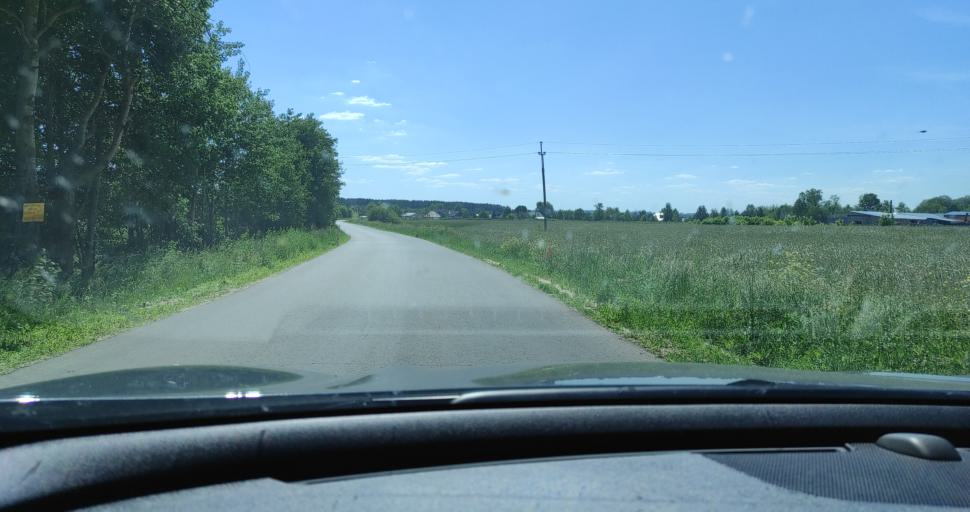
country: RU
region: Rjazan
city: Murmino
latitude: 54.5691
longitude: 40.0963
